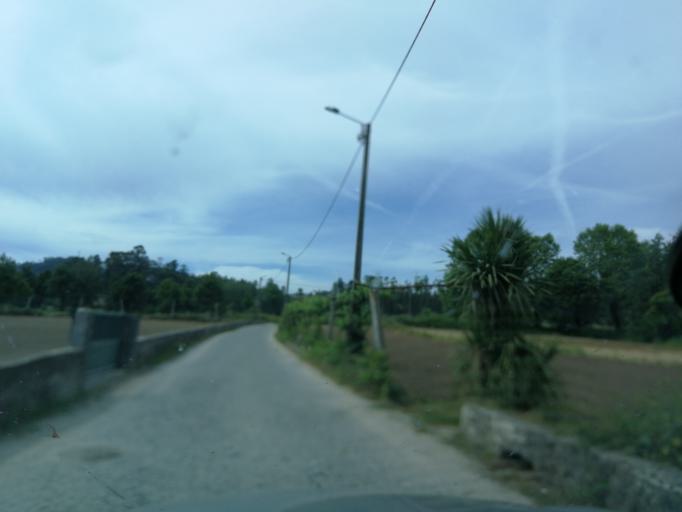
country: PT
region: Braga
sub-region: Braga
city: Oliveira
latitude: 41.4703
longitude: -8.4806
